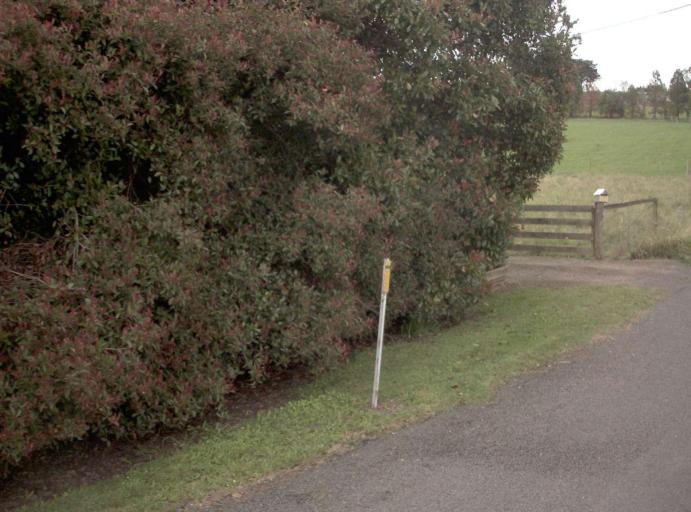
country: AU
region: Victoria
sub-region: Baw Baw
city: Warragul
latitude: -38.1116
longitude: 145.9768
